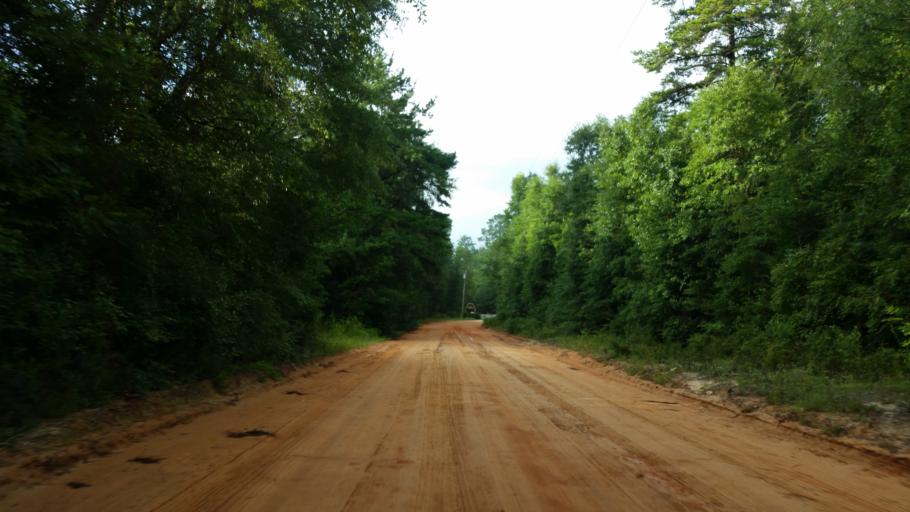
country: US
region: Florida
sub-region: Okaloosa County
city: Crestview
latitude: 30.6716
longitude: -86.7568
